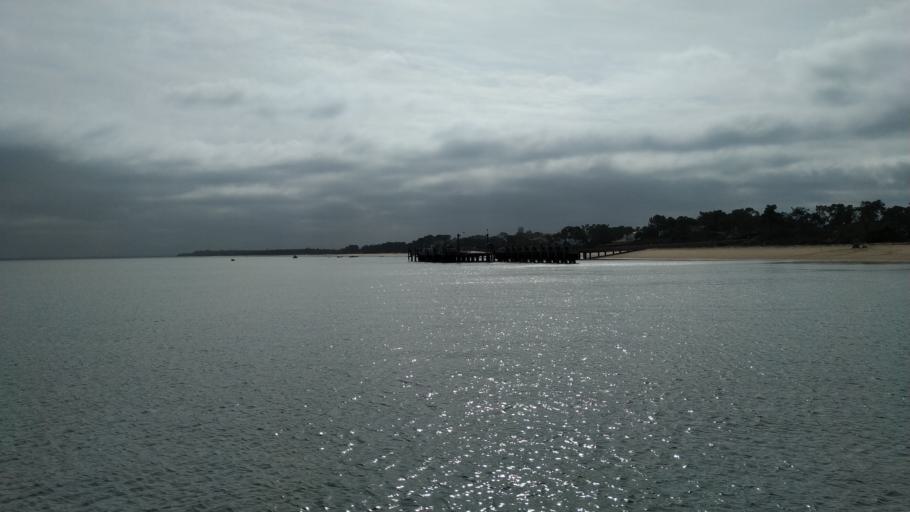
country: PT
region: Setubal
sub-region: Setubal
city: Setubal
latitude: 38.4695
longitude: -8.8645
